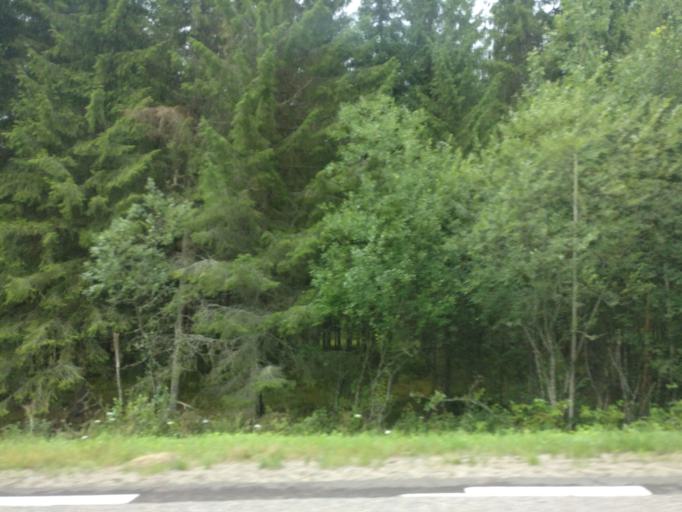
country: SE
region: Vaermland
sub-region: Torsby Kommun
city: Torsby
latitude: 60.7672
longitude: 12.7586
